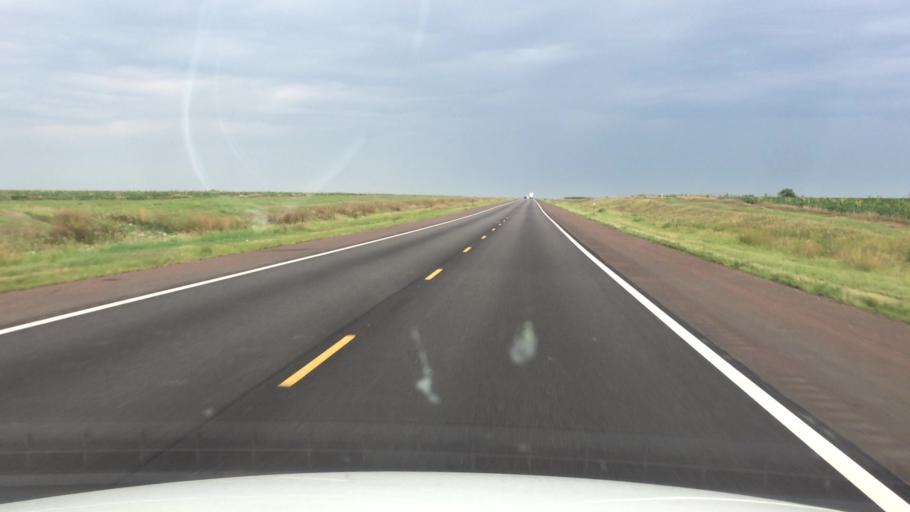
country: US
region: Kansas
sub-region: Nemaha County
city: Sabetha
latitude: 39.8592
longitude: -95.7605
